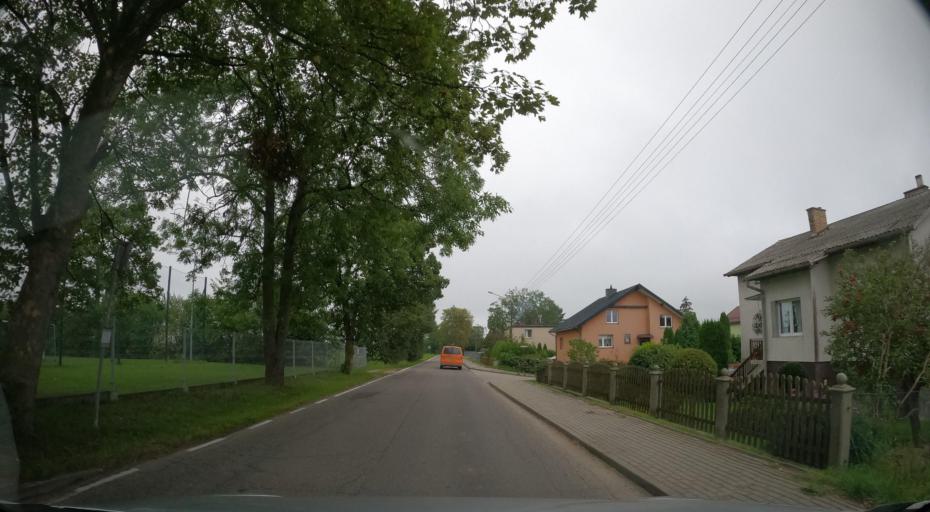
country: PL
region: Pomeranian Voivodeship
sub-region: Powiat wejherowski
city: Szemud
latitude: 54.5020
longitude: 18.1521
